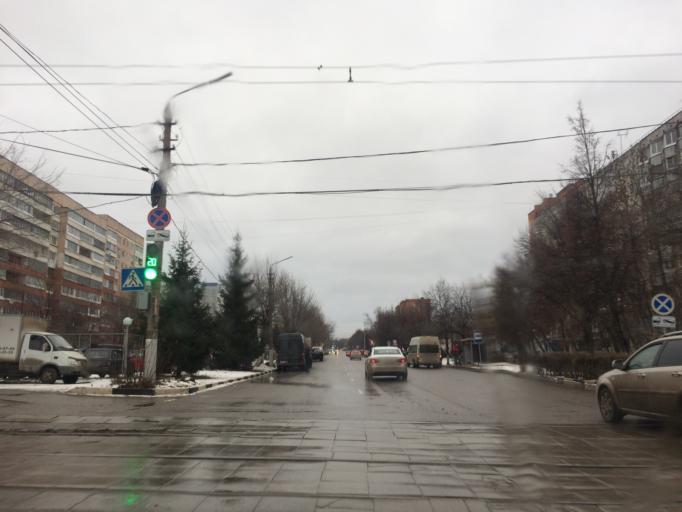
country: RU
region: Tula
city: Tula
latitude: 54.1986
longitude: 37.6476
